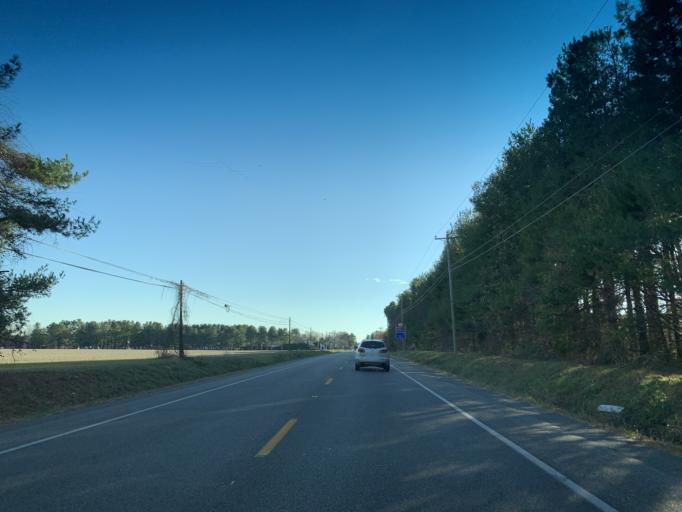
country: US
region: Delaware
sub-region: New Castle County
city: Middletown
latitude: 39.3525
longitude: -75.8775
